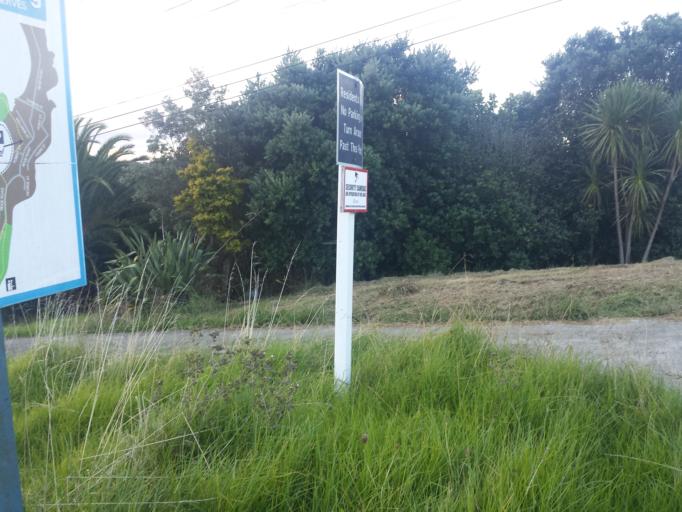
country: NZ
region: Auckland
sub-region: Auckland
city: Warkworth
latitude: -36.4751
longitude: 174.7326
